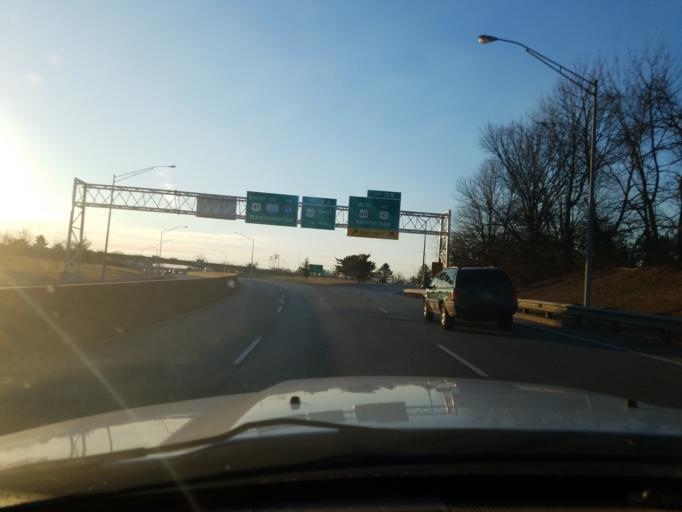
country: US
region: Kentucky
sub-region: Henderson County
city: Henderson
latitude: 37.8594
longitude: -87.5753
